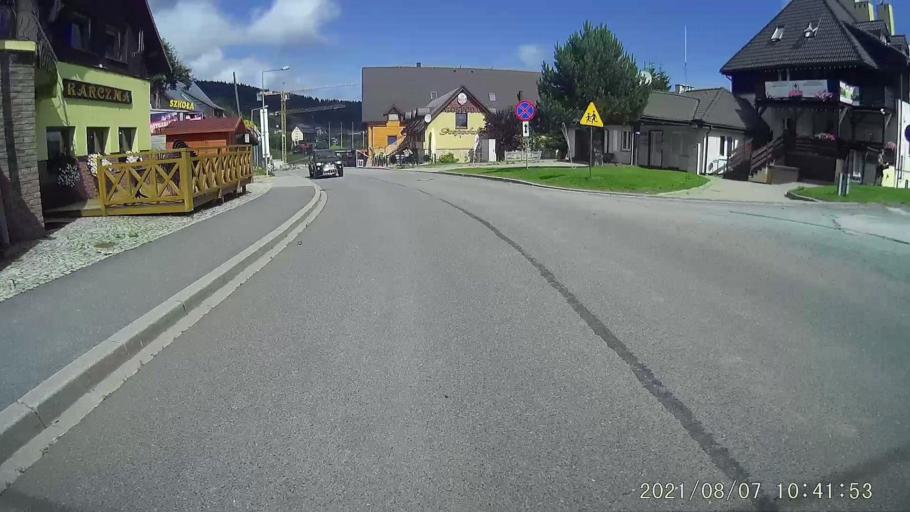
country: PL
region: Lower Silesian Voivodeship
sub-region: Powiat klodzki
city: Duszniki-Zdroj
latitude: 50.3356
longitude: 16.3888
